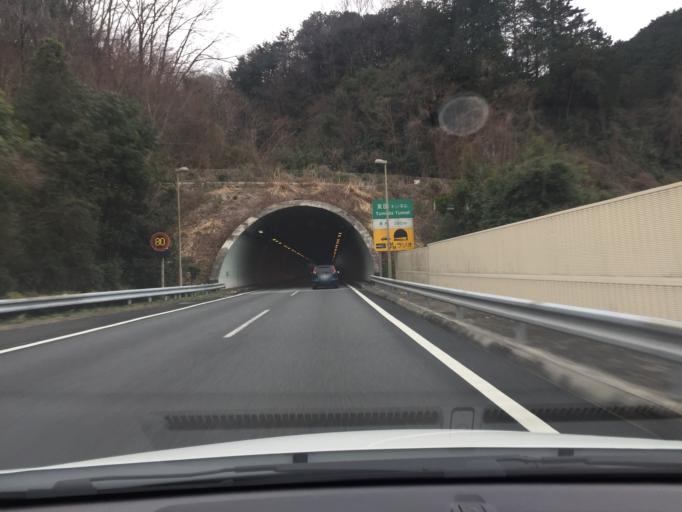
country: JP
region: Tokyo
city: Fussa
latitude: 35.7697
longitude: 139.2897
